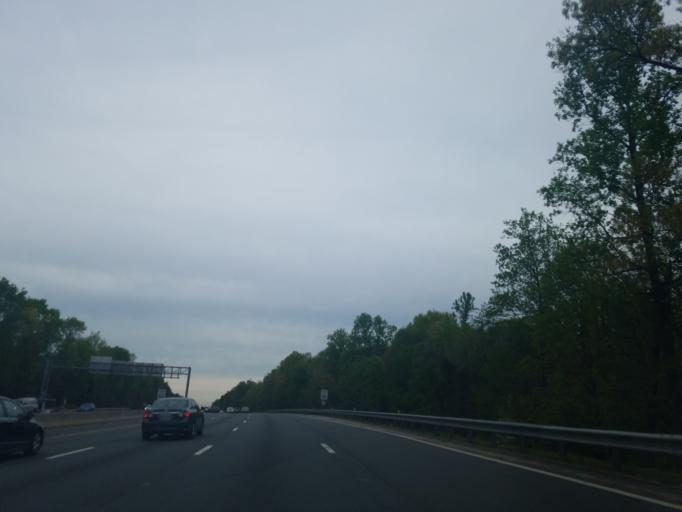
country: US
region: Virginia
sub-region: Fairfax County
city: Centreville
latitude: 38.8556
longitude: -77.4333
